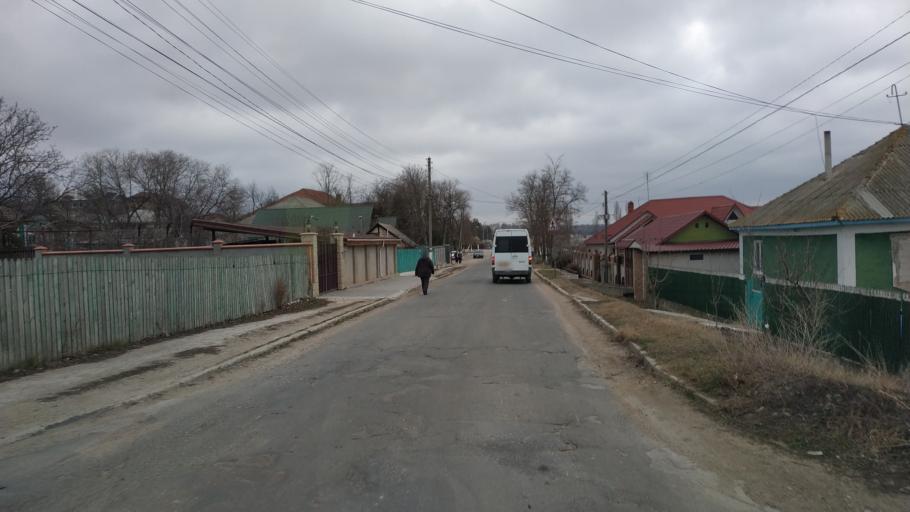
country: MD
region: Laloveni
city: Ialoveni
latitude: 46.9067
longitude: 28.8083
